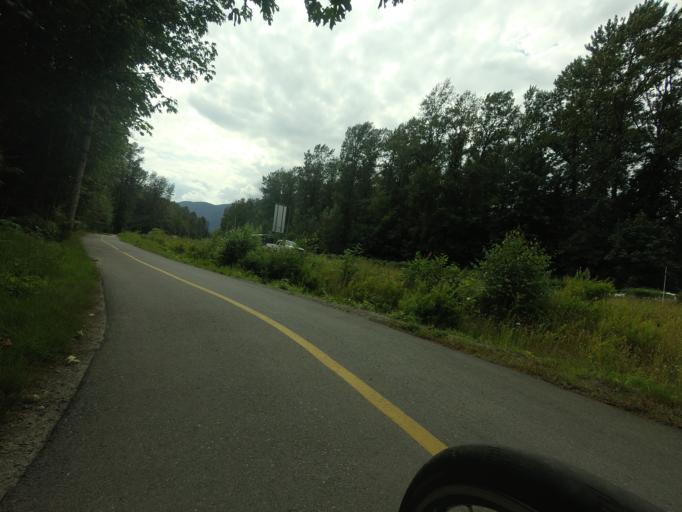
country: CA
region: British Columbia
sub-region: Greater Vancouver Regional District
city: Lions Bay
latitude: 49.7318
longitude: -123.1352
